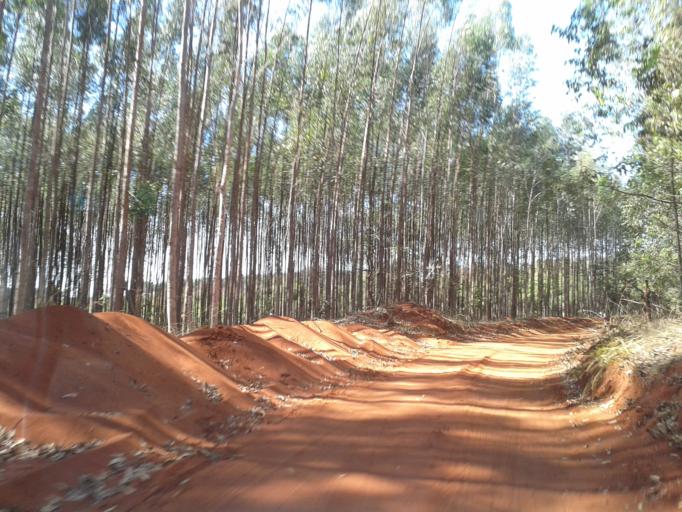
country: BR
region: Minas Gerais
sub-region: Ituiutaba
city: Ituiutaba
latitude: -19.0117
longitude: -49.2202
